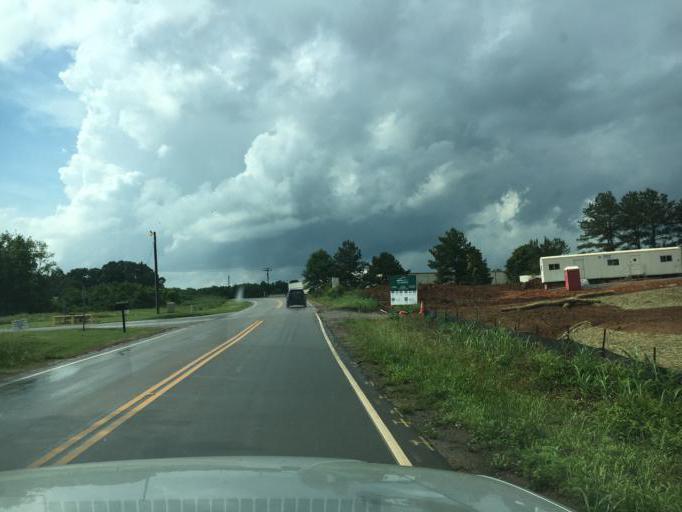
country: US
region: South Carolina
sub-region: Spartanburg County
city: Wellford
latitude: 34.9316
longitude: -82.0628
